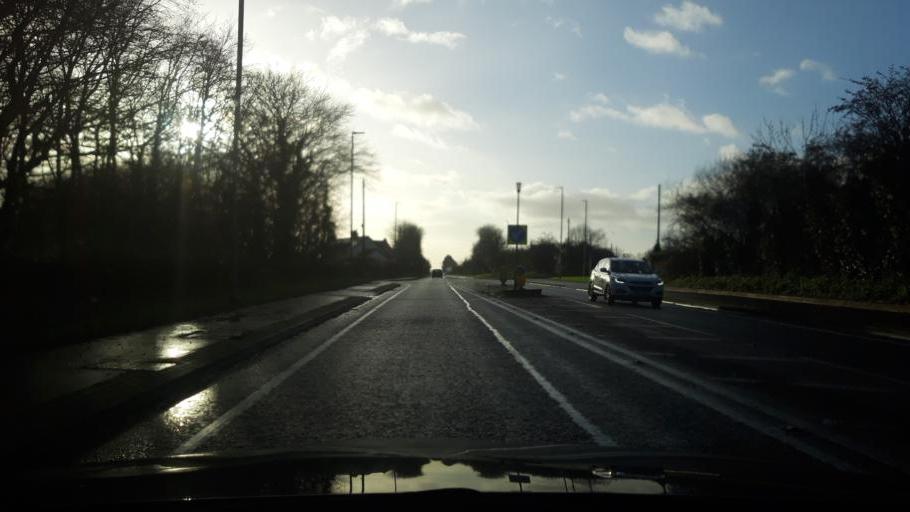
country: GB
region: Northern Ireland
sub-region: Coleraine District
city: Coleraine
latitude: 55.1154
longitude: -6.6857
